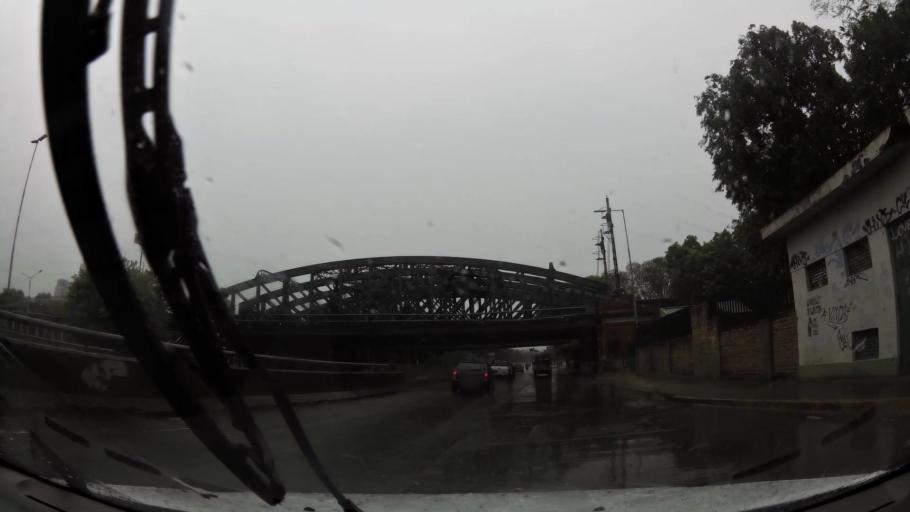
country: AR
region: Buenos Aires F.D.
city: Retiro
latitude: -34.5681
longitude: -58.4088
